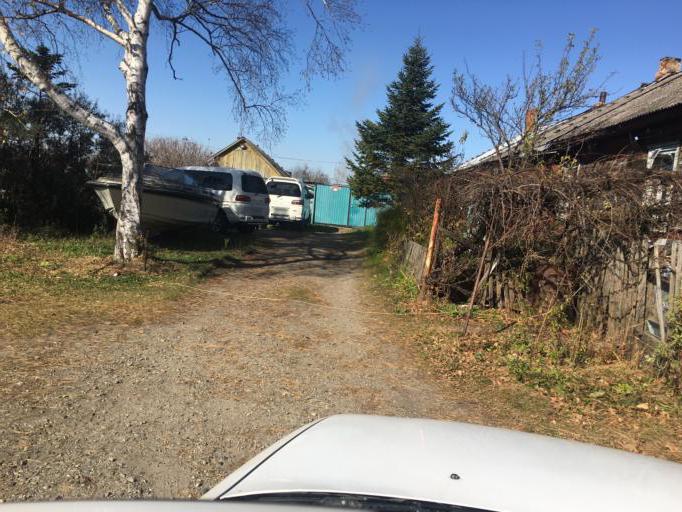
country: RU
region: Primorskiy
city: Dal'nerechensk
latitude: 45.9125
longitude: 133.7908
